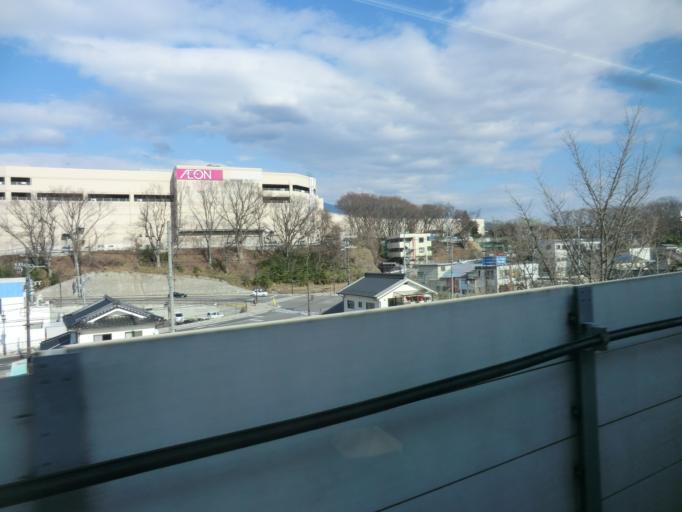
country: JP
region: Nagano
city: Ueda
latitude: 36.3913
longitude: 138.2557
